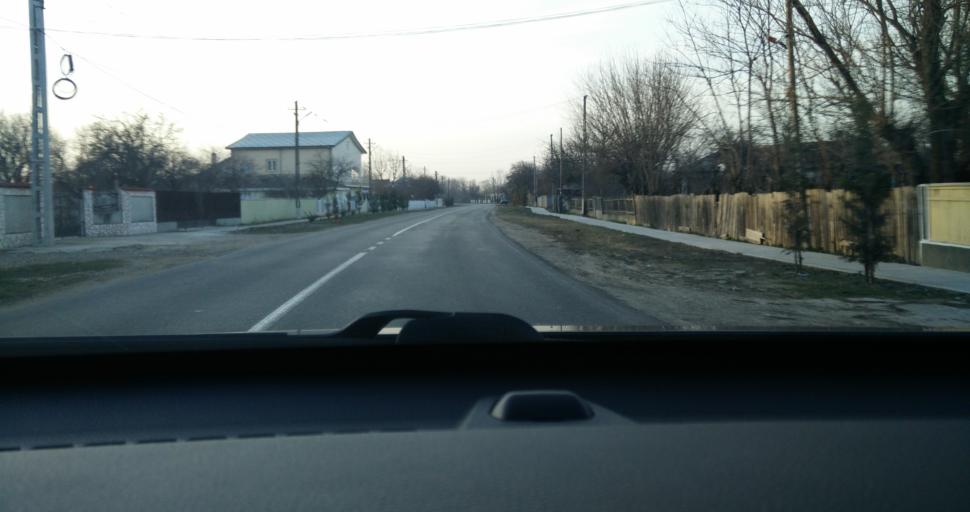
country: RO
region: Vrancea
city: Vulturu de Sus
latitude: 45.6287
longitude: 27.3913
